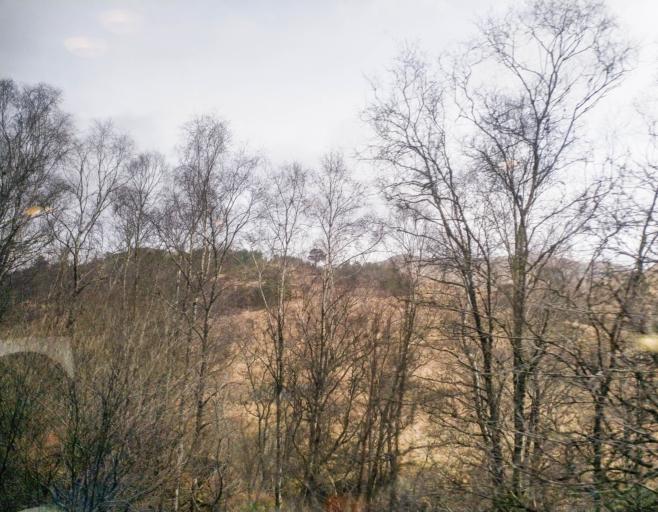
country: GB
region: Scotland
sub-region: Argyll and Bute
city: Garelochhead
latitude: 56.3735
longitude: -4.6506
